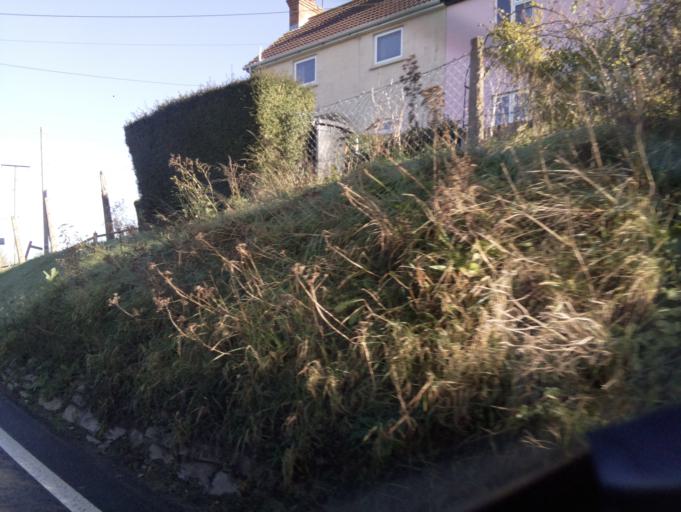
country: GB
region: England
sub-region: Somerset
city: Langport
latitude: 51.0619
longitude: -2.8580
